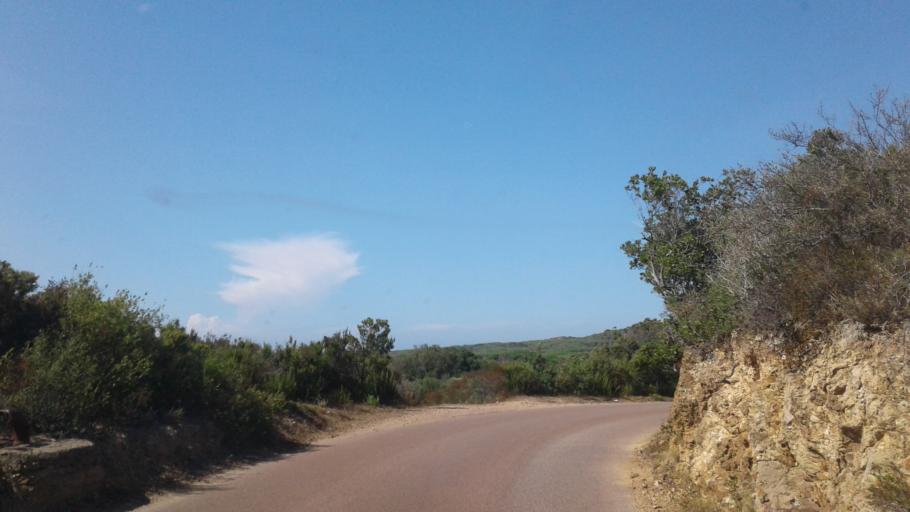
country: IT
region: Sardinia
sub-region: Provincia di Olbia-Tempio
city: La Maddalena
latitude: 41.1935
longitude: 9.4560
